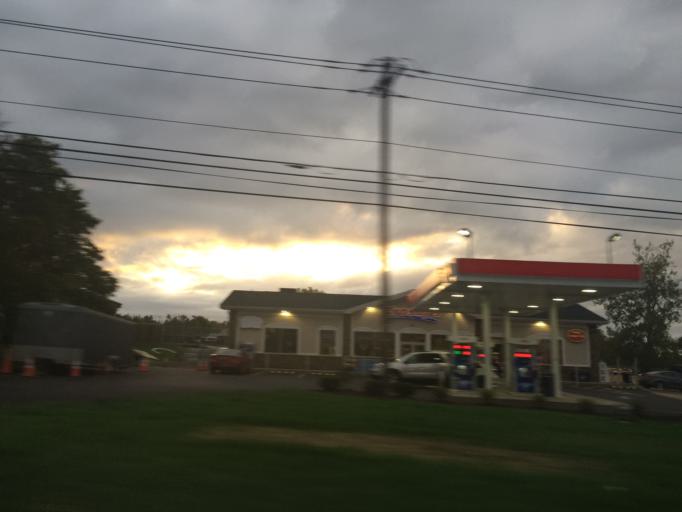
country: US
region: New York
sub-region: Erie County
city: Billington Heights
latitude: 42.7942
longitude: -78.6215
